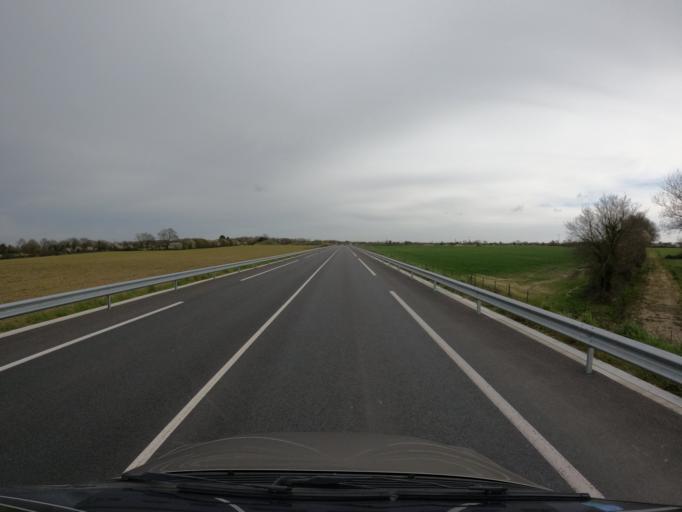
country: FR
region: Pays de la Loire
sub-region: Departement de la Vendee
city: Montaigu
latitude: 46.9854
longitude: -1.2975
